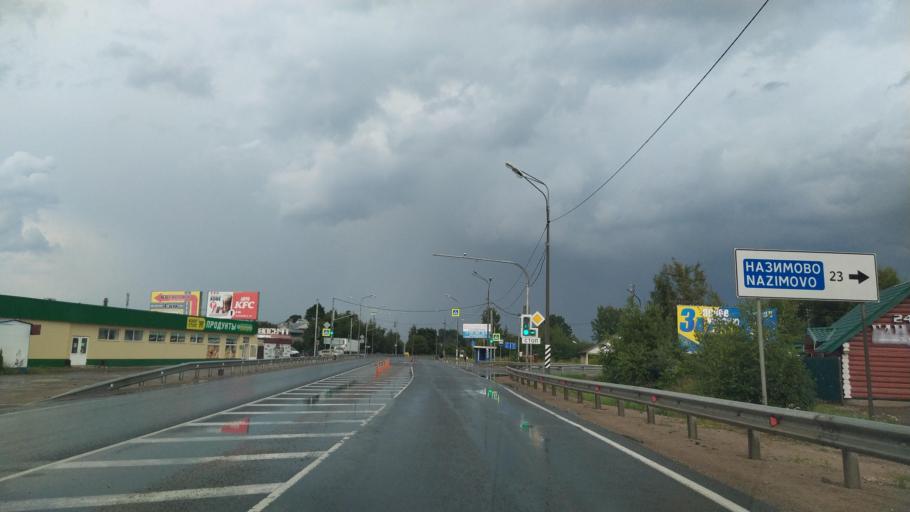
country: RU
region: Pskov
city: Pskov
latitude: 57.7440
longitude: 28.3702
